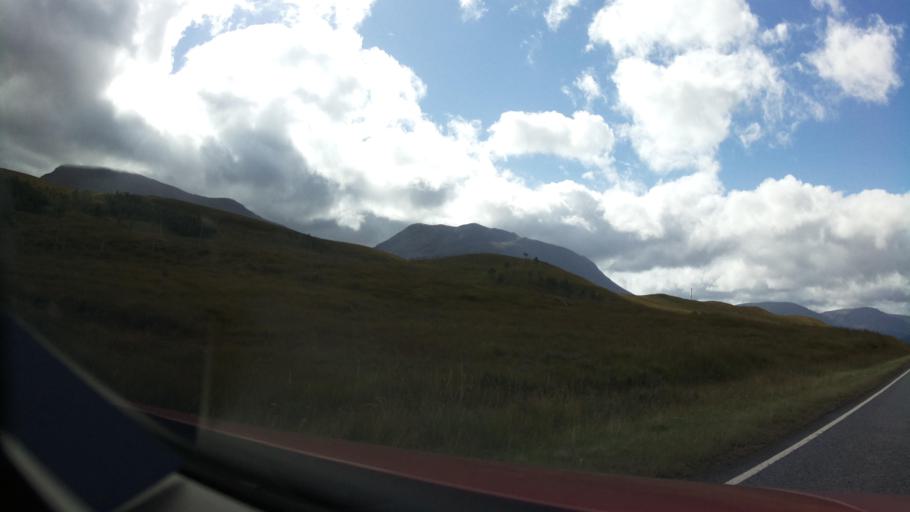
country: GB
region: Scotland
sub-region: Highland
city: Spean Bridge
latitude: 56.5773
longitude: -4.7533
